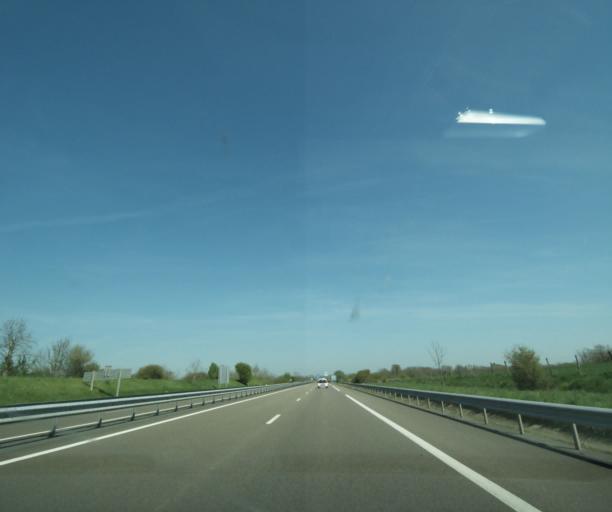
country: FR
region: Bourgogne
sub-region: Departement de la Nievre
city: Sermoise-sur-Loire
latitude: 46.9499
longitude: 3.1672
